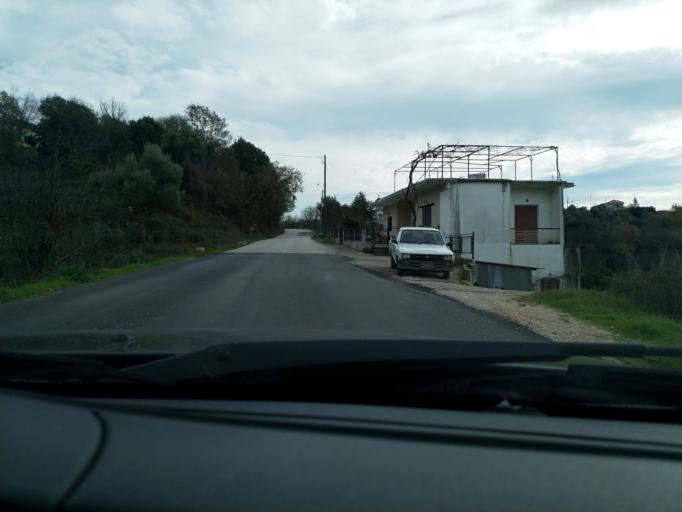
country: GR
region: Epirus
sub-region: Nomos Prevezis
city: Filippiada
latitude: 39.2219
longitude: 20.8496
